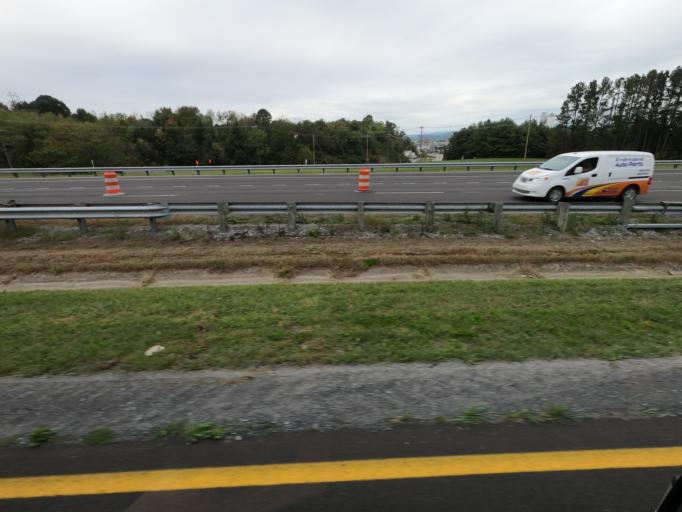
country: US
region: Tennessee
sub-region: Sullivan County
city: Kingsport
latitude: 36.5085
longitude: -82.5458
